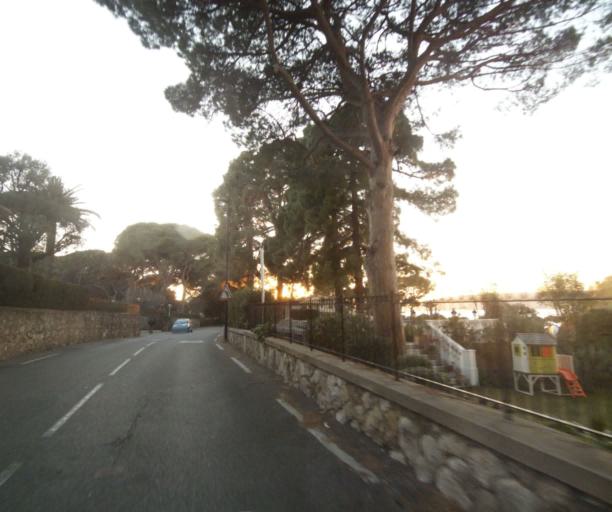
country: FR
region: Provence-Alpes-Cote d'Azur
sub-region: Departement des Alpes-Maritimes
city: Antibes
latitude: 43.5500
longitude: 7.1245
